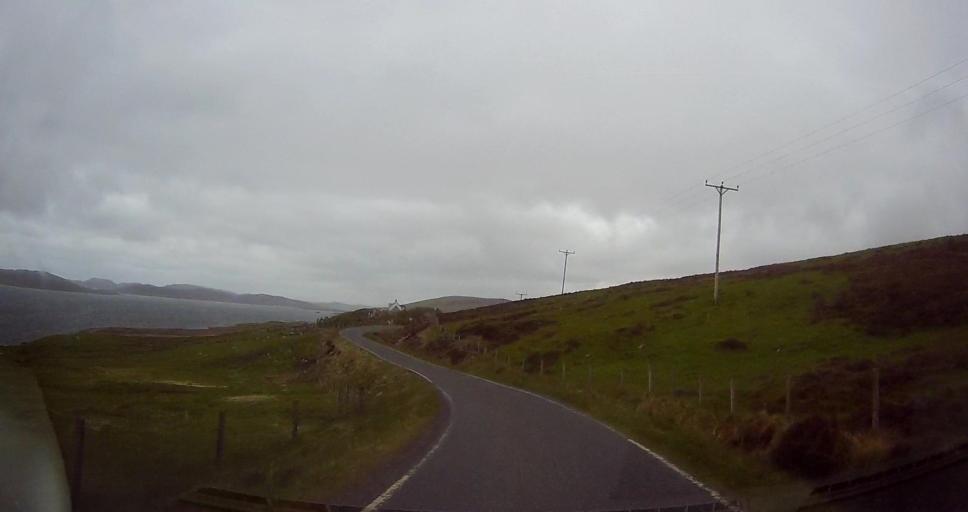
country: GB
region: Scotland
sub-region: Shetland Islands
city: Lerwick
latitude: 60.2922
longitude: -1.3644
